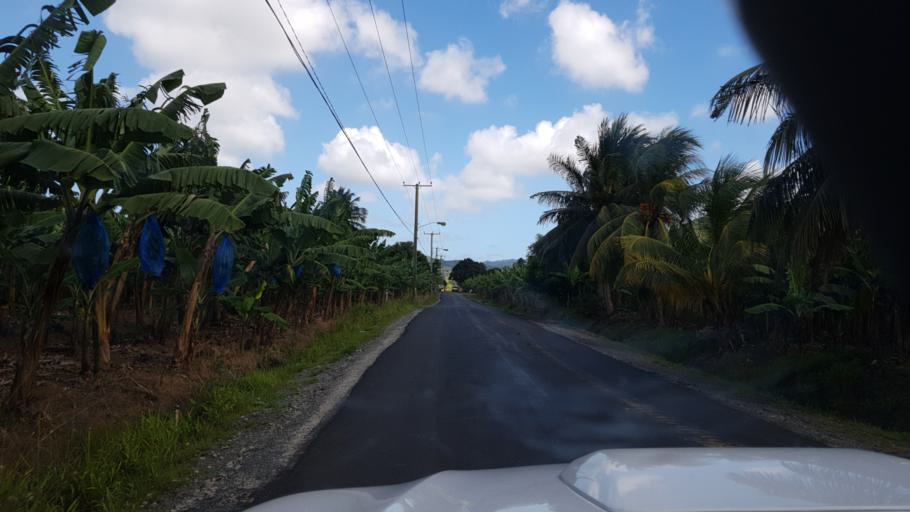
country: LC
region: Anse-la-Raye
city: Anse La Raye
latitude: 13.9538
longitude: -61.0191
